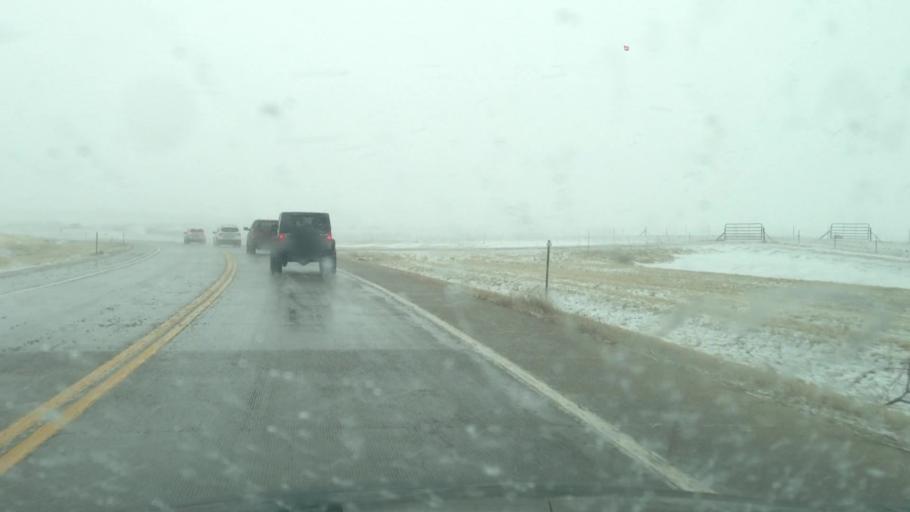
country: US
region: Colorado
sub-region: Park County
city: Castle Pines North
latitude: 39.4820
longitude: -104.8604
